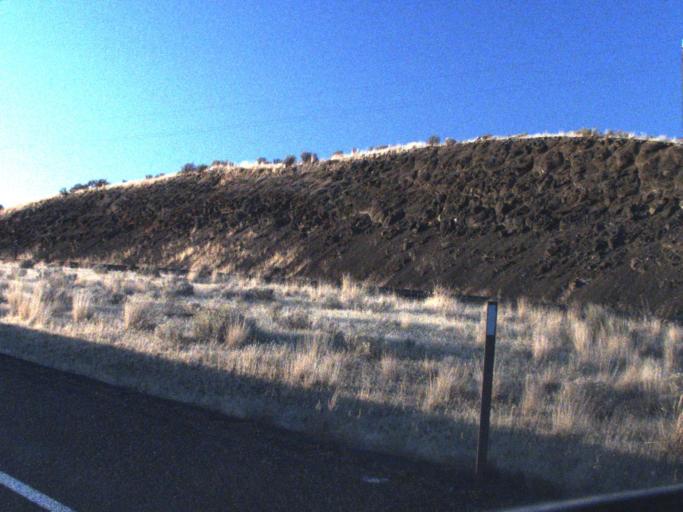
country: US
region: Washington
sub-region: Adams County
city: Ritzville
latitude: 46.9692
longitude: -118.5623
